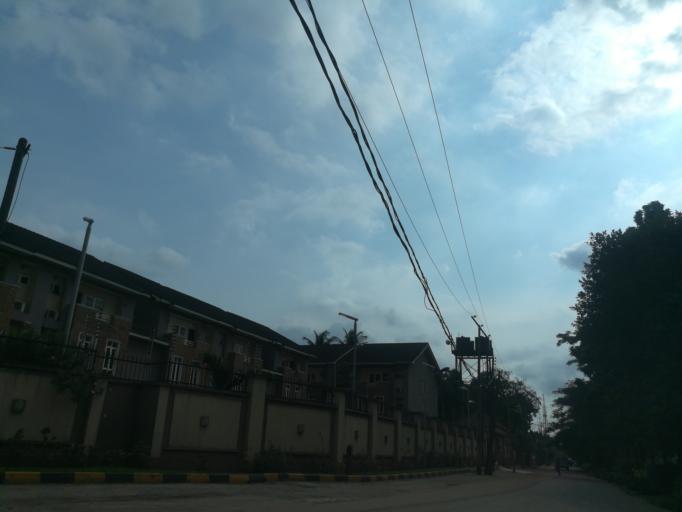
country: NG
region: Lagos
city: Oshodi
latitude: 6.5772
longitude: 3.3553
